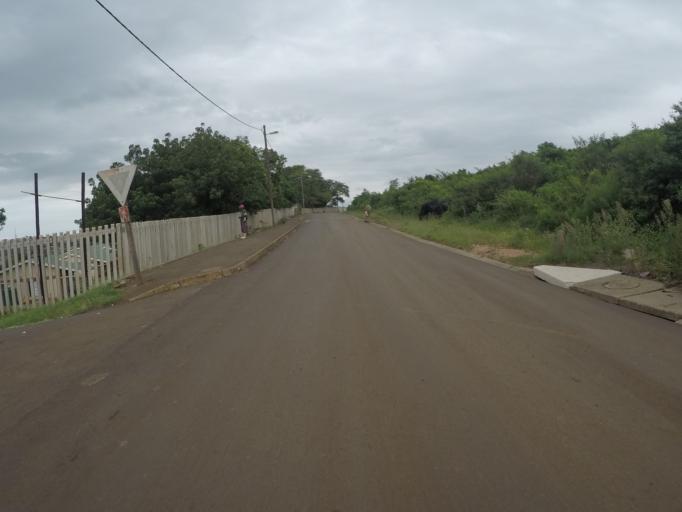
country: ZA
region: KwaZulu-Natal
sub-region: uThungulu District Municipality
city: Empangeni
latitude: -28.7702
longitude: 31.8603
